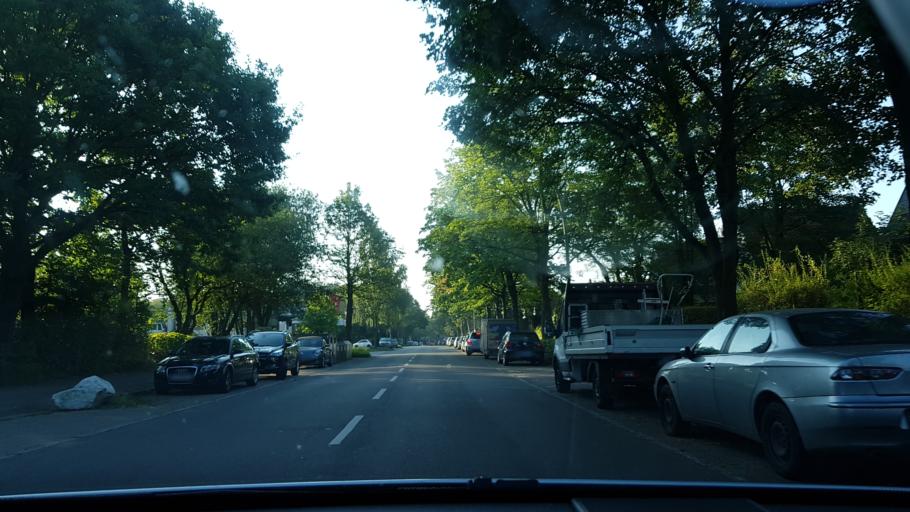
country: DE
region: Hamburg
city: Farmsen-Berne
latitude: 53.6286
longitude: 10.1663
